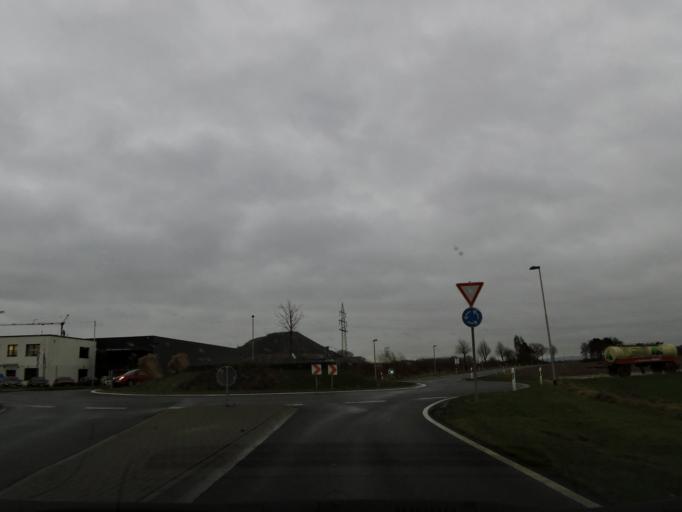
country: DE
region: North Rhine-Westphalia
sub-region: Regierungsbezirk Koln
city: Herzogenrath
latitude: 50.8788
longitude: 6.1150
